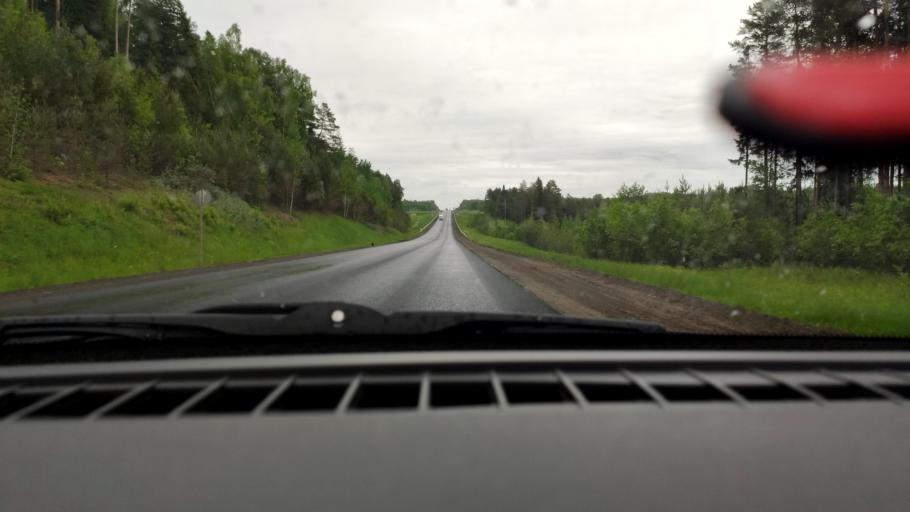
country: RU
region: Perm
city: Karagay
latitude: 58.2525
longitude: 54.9088
